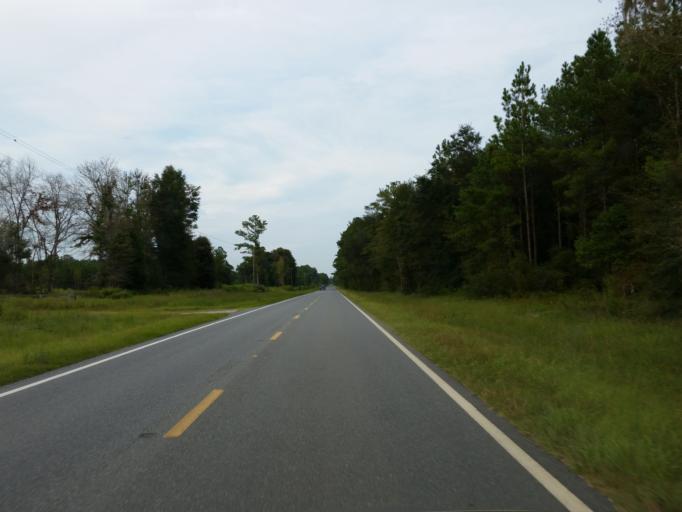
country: US
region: Georgia
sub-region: Echols County
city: Statenville
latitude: 30.5759
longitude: -83.1459
